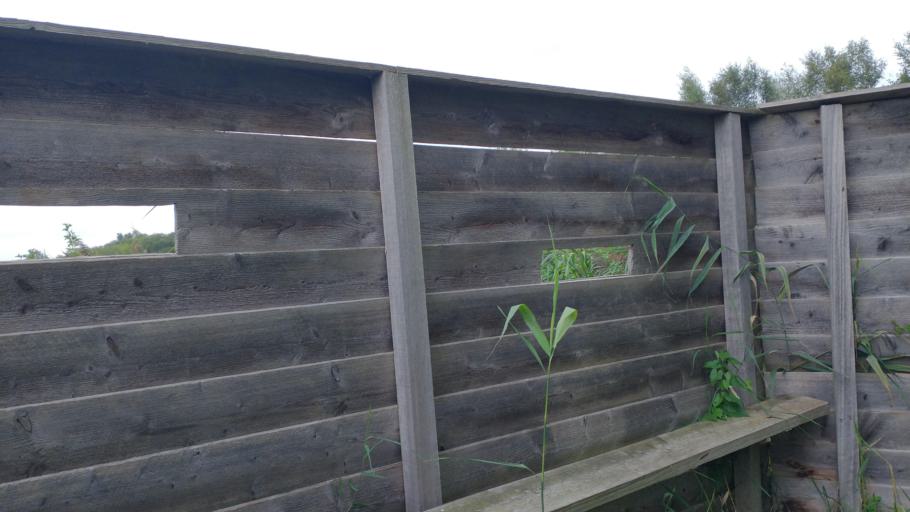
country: NL
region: Overijssel
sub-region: Gemeente Steenwijkerland
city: Giethoorn
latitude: 52.7301
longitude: 6.0465
